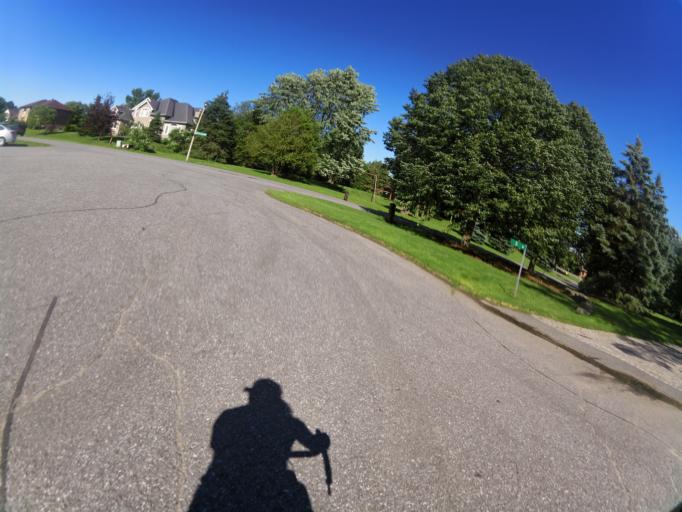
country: CA
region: Ontario
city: Bells Corners
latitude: 45.2628
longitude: -75.8263
